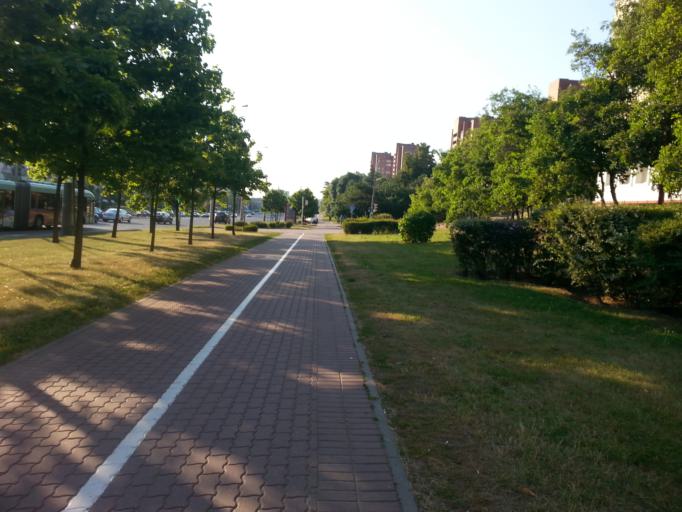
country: BY
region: Minsk
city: Vyaliki Trastsyanets
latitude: 53.8658
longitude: 27.6594
